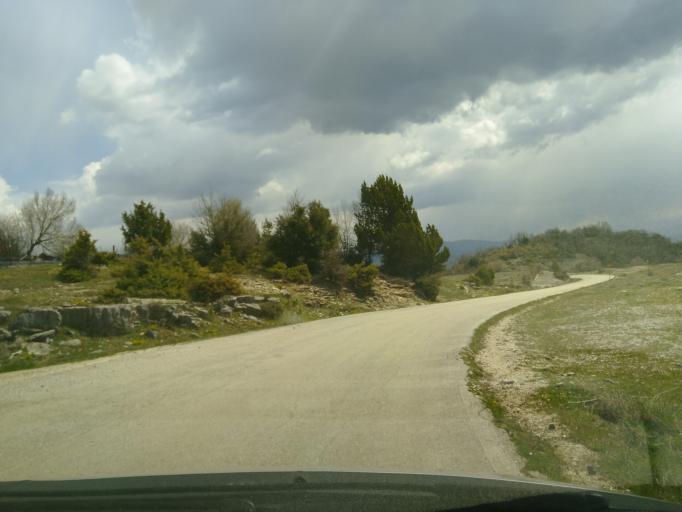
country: GR
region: Epirus
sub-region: Nomos Ioanninon
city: Asprangeloi
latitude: 39.8805
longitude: 20.7352
